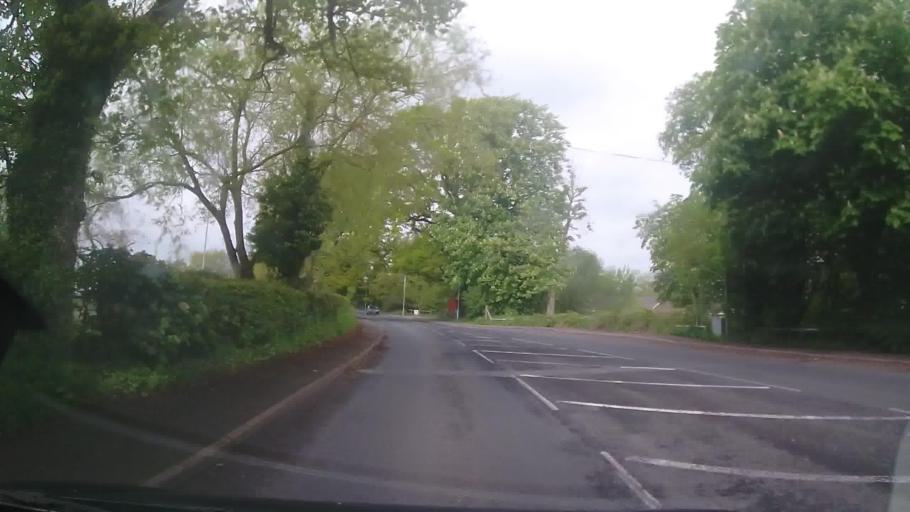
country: GB
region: England
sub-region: Shropshire
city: Ellesmere
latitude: 52.9523
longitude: -2.8687
